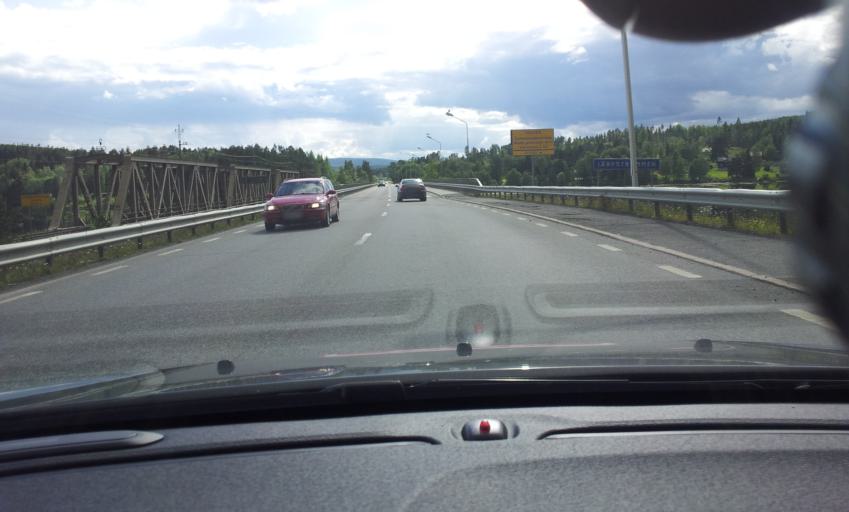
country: SE
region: Jaemtland
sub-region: Are Kommun
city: Jarpen
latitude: 63.3453
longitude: 13.4566
